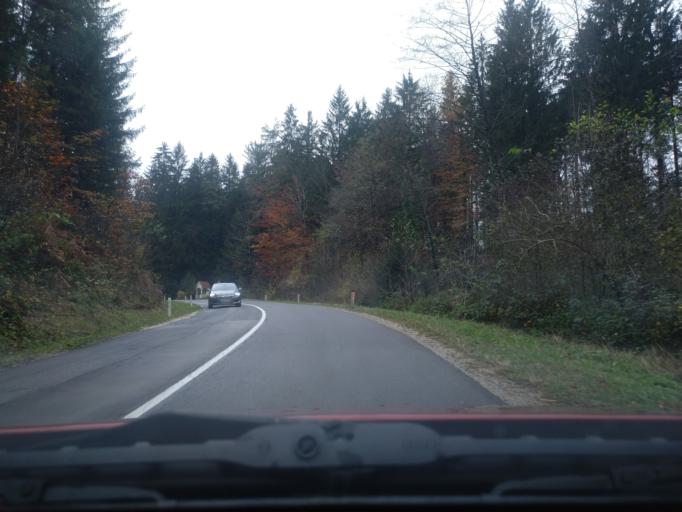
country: SI
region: Ljubno
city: Ljubno ob Savinji
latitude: 46.3113
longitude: 14.8397
